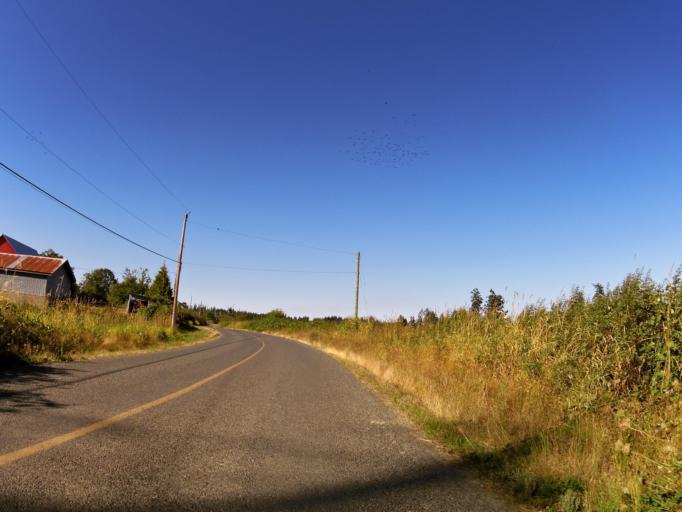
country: CA
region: British Columbia
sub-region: Cowichan Valley Regional District
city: Ladysmith
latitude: 49.0827
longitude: -123.8437
